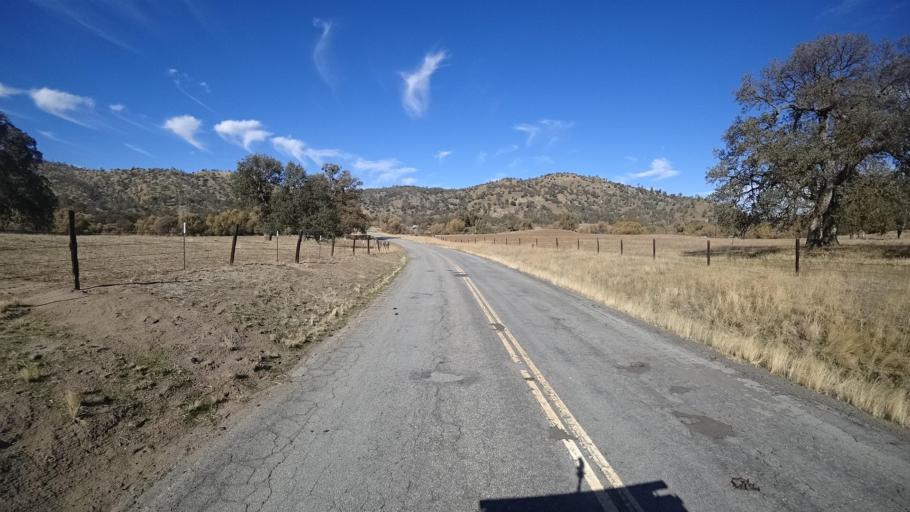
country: US
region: California
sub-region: Kern County
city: Alta Sierra
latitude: 35.6254
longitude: -118.7472
